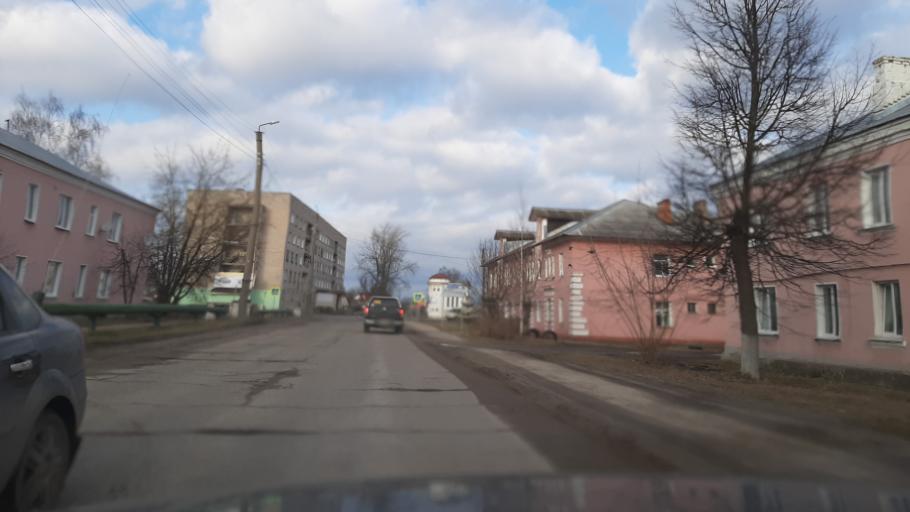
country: RU
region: Ivanovo
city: Teykovo
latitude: 56.8582
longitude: 40.5563
